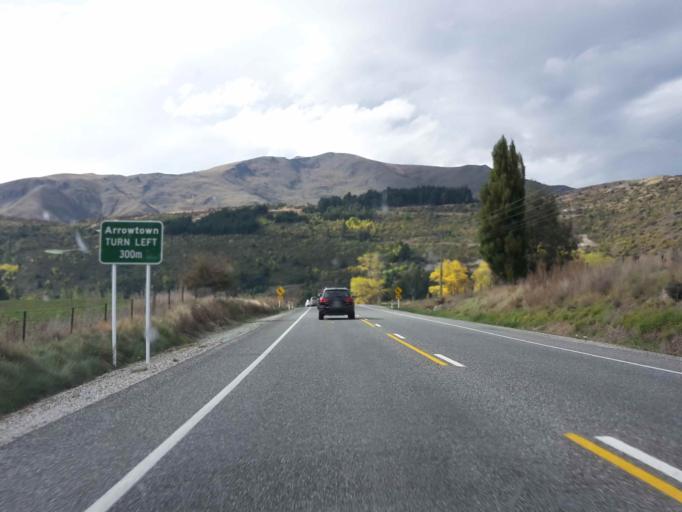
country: NZ
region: Otago
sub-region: Queenstown-Lakes District
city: Arrowtown
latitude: -44.9794
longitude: 168.8452
